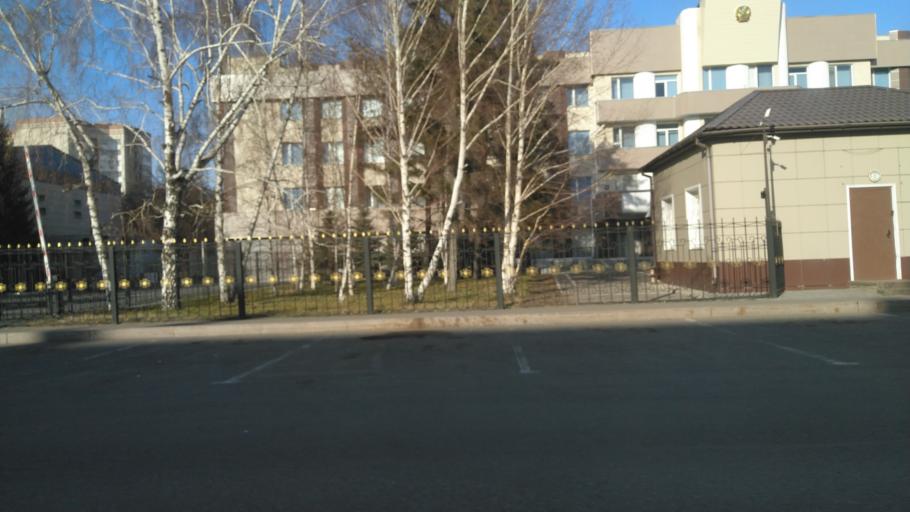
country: KZ
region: Pavlodar
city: Pavlodar
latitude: 52.2907
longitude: 76.9462
